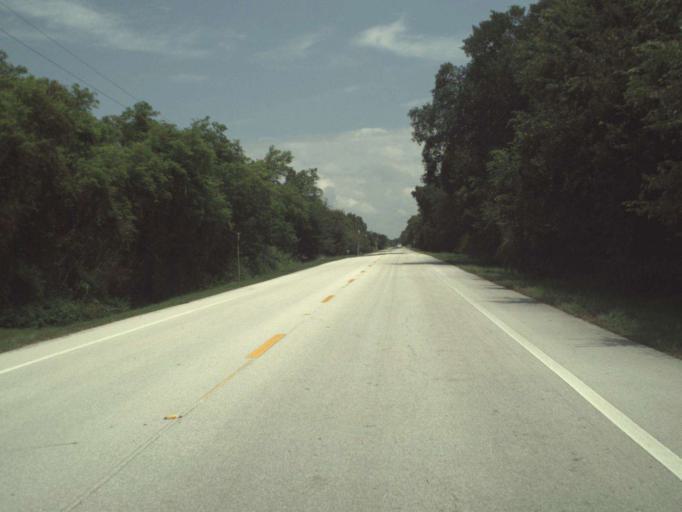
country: US
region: Florida
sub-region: Martin County
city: Indiantown
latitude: 27.0306
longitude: -80.6344
